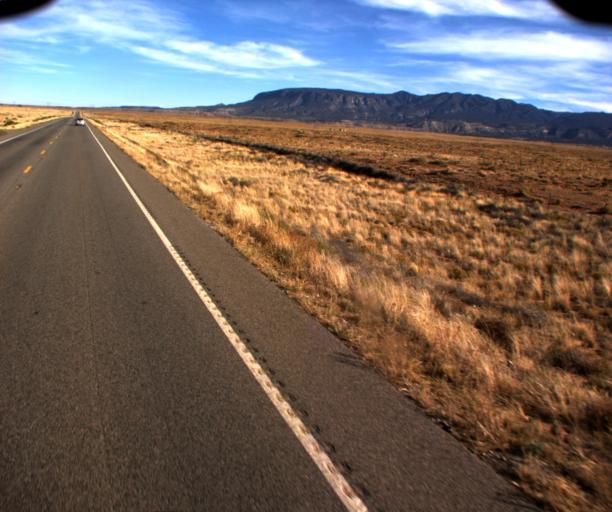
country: US
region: Arizona
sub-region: Apache County
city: Lukachukai
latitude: 36.9441
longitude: -109.2626
